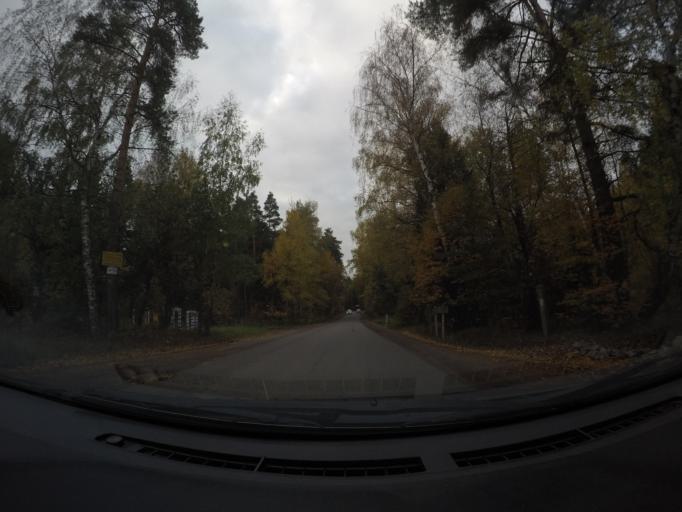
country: RU
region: Moskovskaya
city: Vishnyakovskiye Dachi
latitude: 55.8111
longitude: 38.1095
